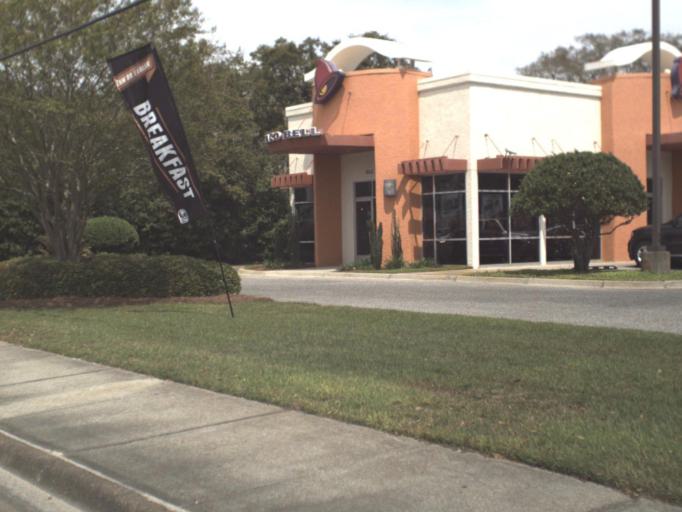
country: US
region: Florida
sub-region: Okaloosa County
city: Wright
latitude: 30.4525
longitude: -86.6384
